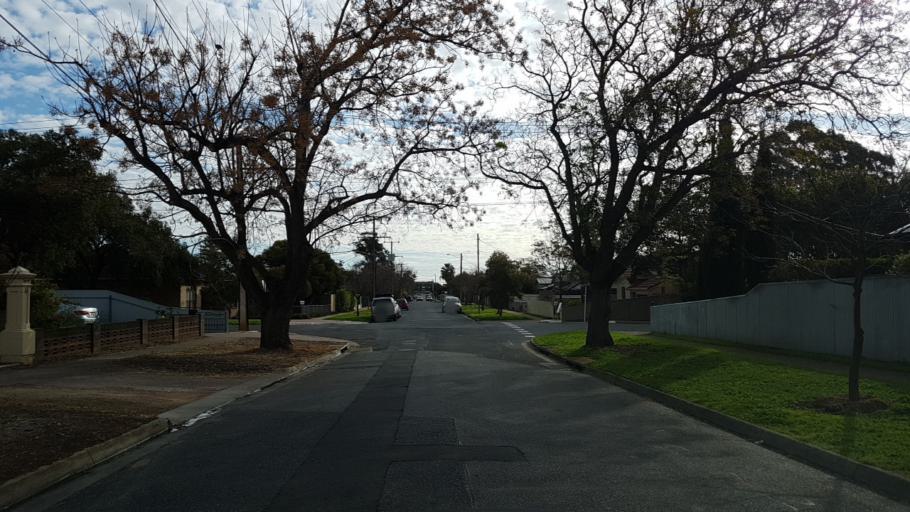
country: AU
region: South Australia
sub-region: Prospect
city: Prospect
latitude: -34.8776
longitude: 138.5897
